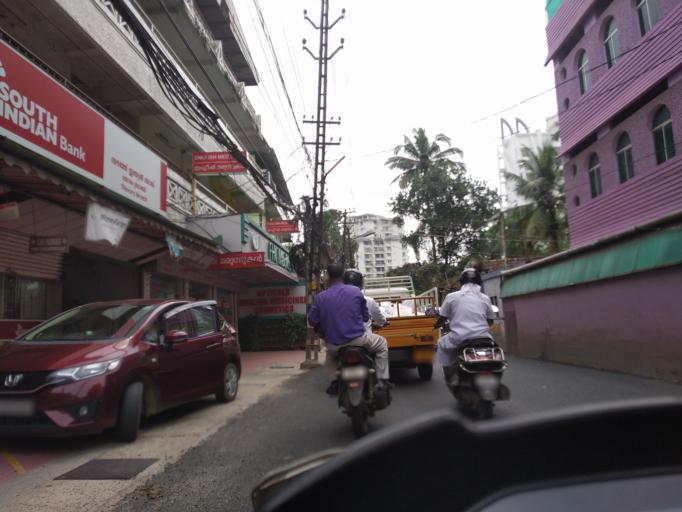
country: IN
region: Kerala
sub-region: Ernakulam
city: Cochin
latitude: 9.9372
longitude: 76.2972
